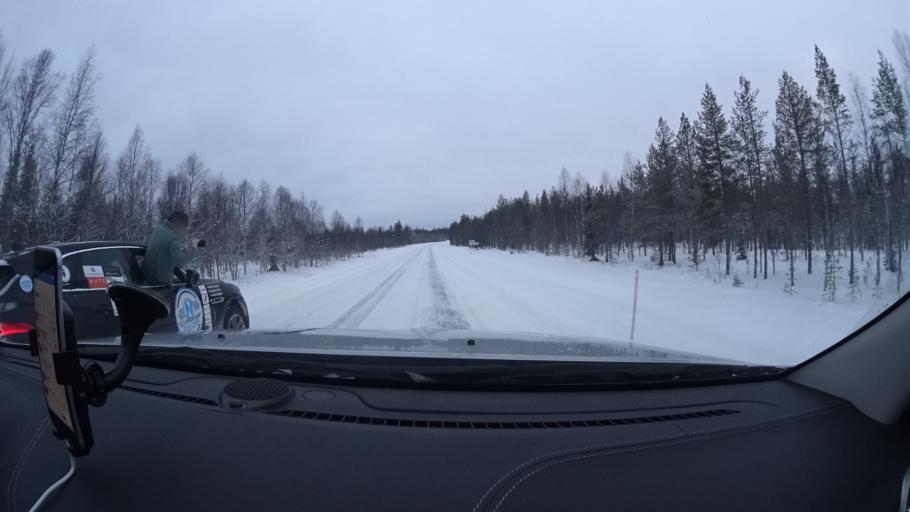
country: FI
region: Lapland
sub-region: Itae-Lappi
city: Posio
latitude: 66.1886
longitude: 27.7659
